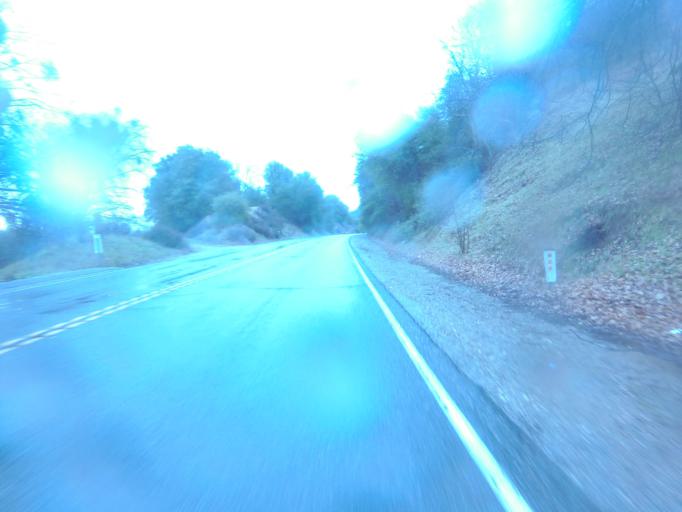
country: US
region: California
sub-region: San Diego County
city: Julian
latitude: 33.2154
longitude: -116.7410
